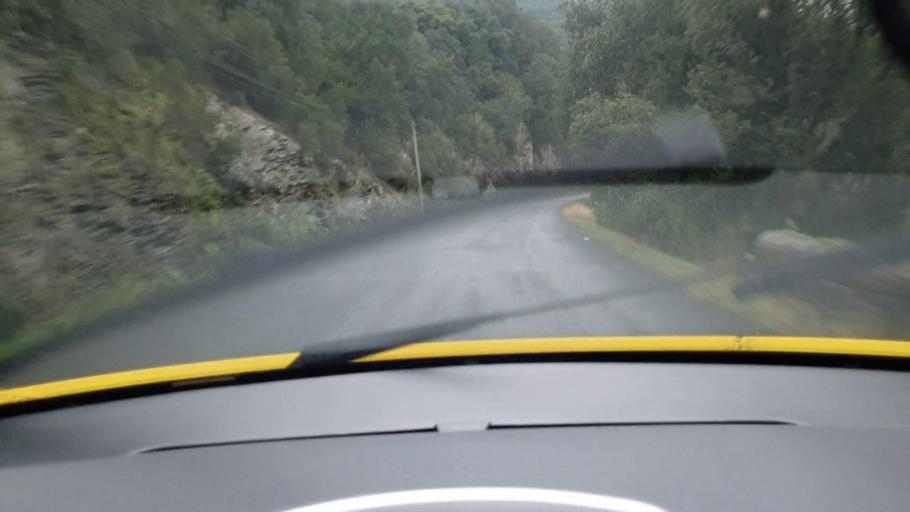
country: FR
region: Languedoc-Roussillon
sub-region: Departement du Gard
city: Sumene
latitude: 43.9982
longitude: 3.7110
